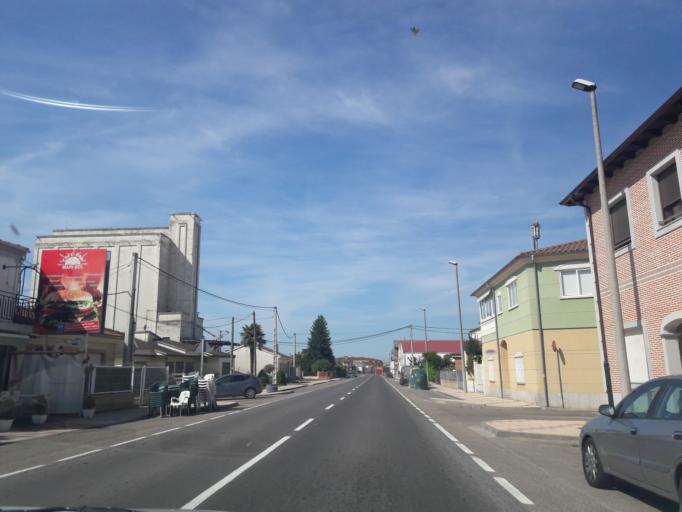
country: ES
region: Castille and Leon
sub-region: Provincia de Salamanca
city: Babilafuente
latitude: 40.9749
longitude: -5.4248
